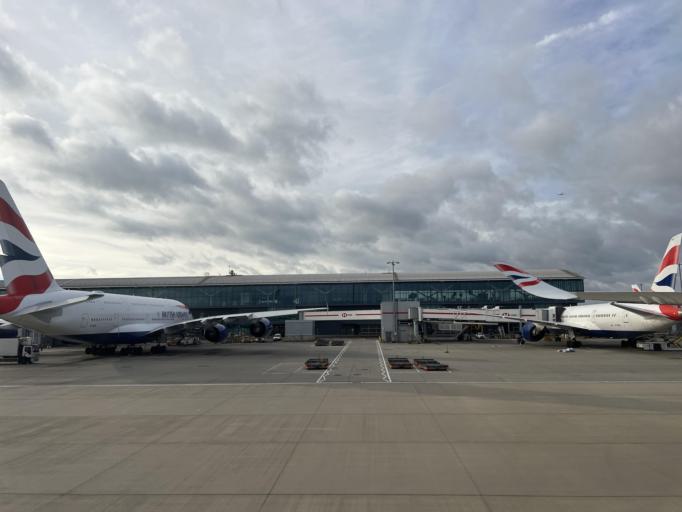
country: GB
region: England
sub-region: Greater London
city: West Drayton
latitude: 51.4718
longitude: -0.4734
